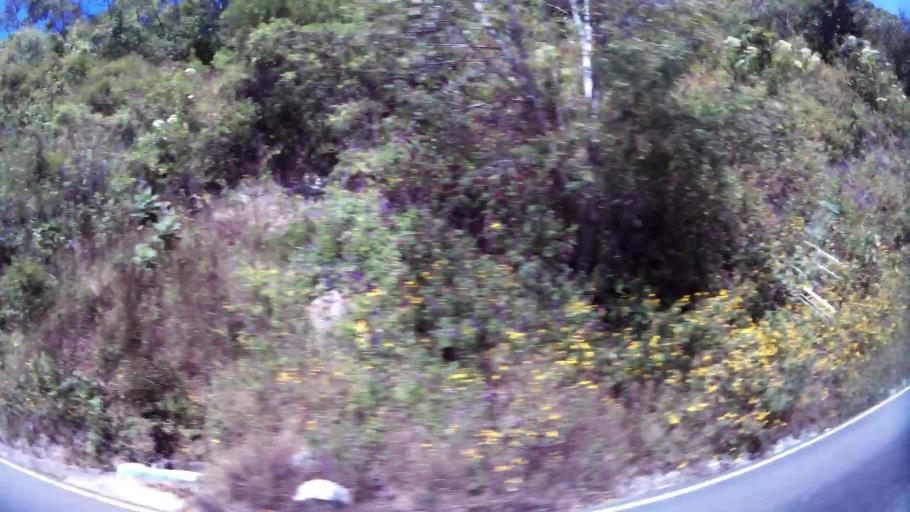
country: GT
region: Solola
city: Solola
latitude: 14.7541
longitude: -91.1758
